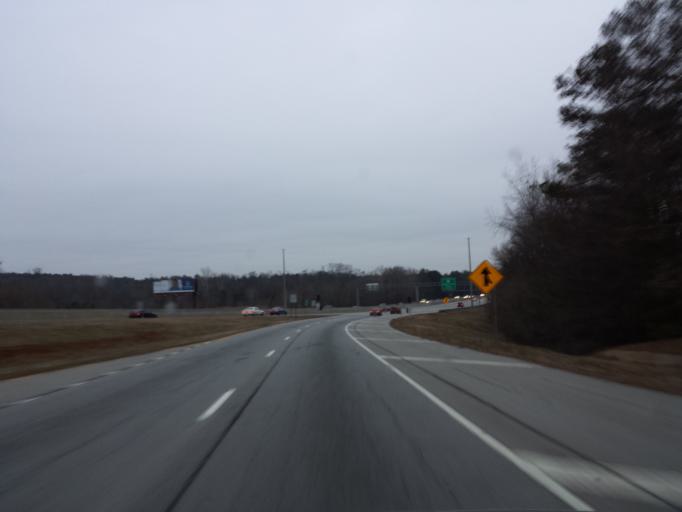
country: US
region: Georgia
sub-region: Fulton County
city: Alpharetta
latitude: 34.0367
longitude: -84.3142
